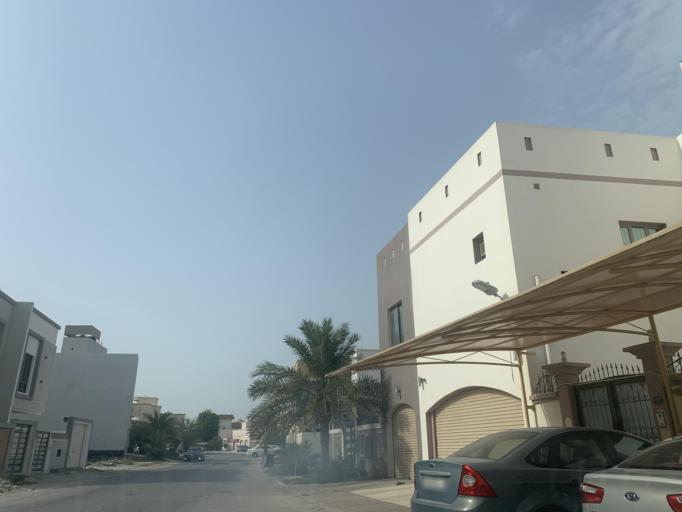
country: BH
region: Northern
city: Madinat `Isa
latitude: 26.1878
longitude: 50.4877
